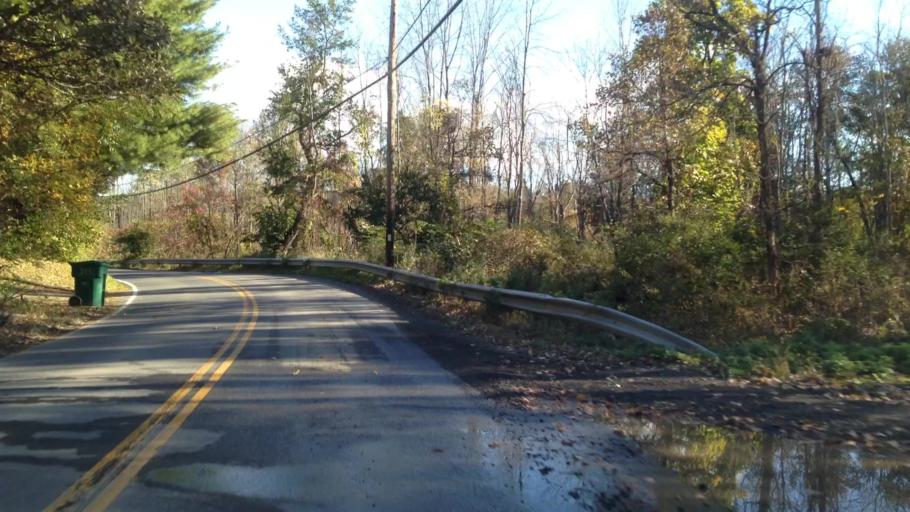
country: US
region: New York
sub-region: Ulster County
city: Port Ewen
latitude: 41.8547
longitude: -73.9846
